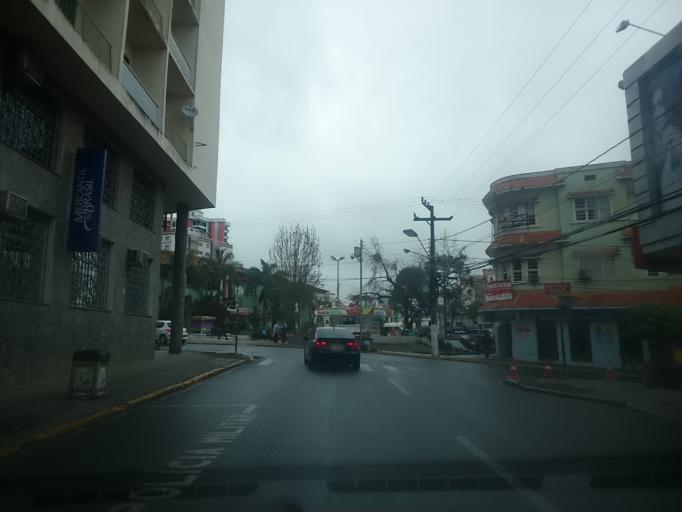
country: BR
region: Santa Catarina
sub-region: Lages
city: Lages
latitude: -27.8146
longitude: -50.3267
